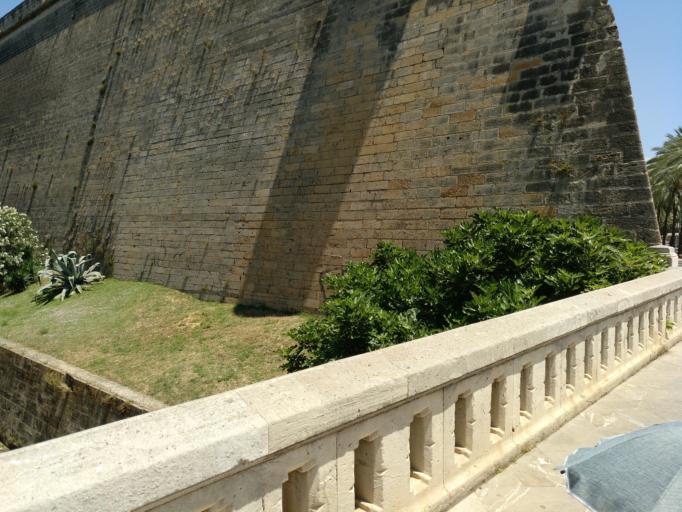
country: ES
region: Balearic Islands
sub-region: Illes Balears
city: Palma
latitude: 39.5699
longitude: 2.6402
